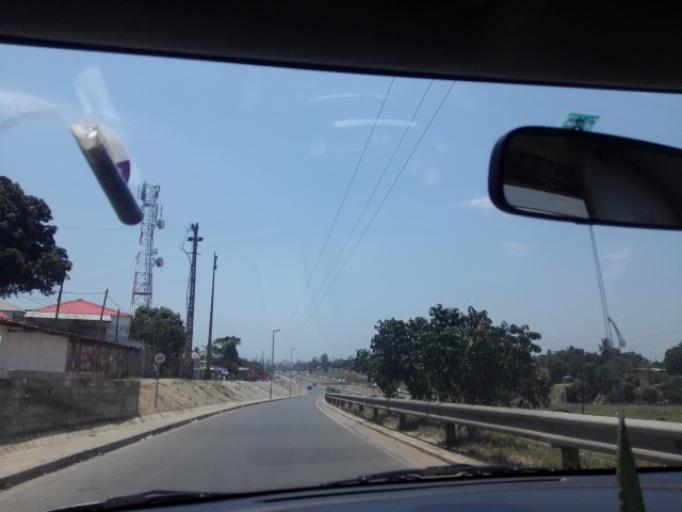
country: MZ
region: Maputo City
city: Maputo
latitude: -25.9286
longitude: 32.5569
